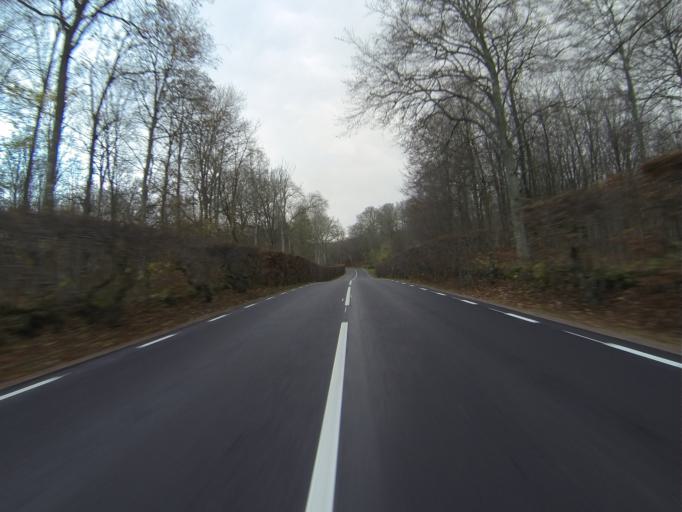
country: SE
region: Skane
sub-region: Lunds Kommun
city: Genarp
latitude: 55.5889
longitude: 13.4197
